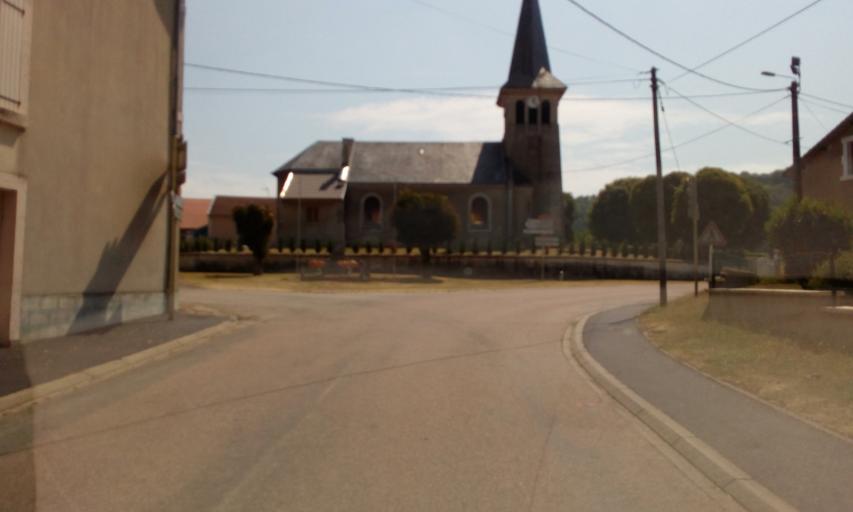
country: FR
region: Lorraine
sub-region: Departement de la Meuse
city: Dieue-sur-Meuse
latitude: 49.1456
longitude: 5.5246
